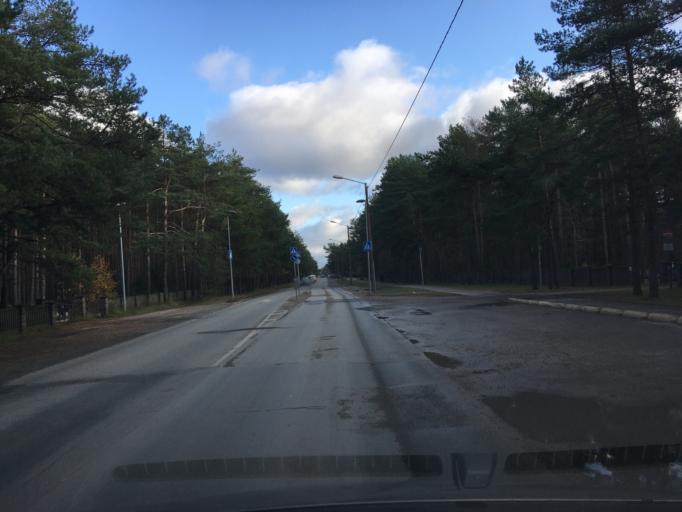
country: EE
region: Harju
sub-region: Tallinna linn
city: Tallinn
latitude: 59.3757
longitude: 24.7289
